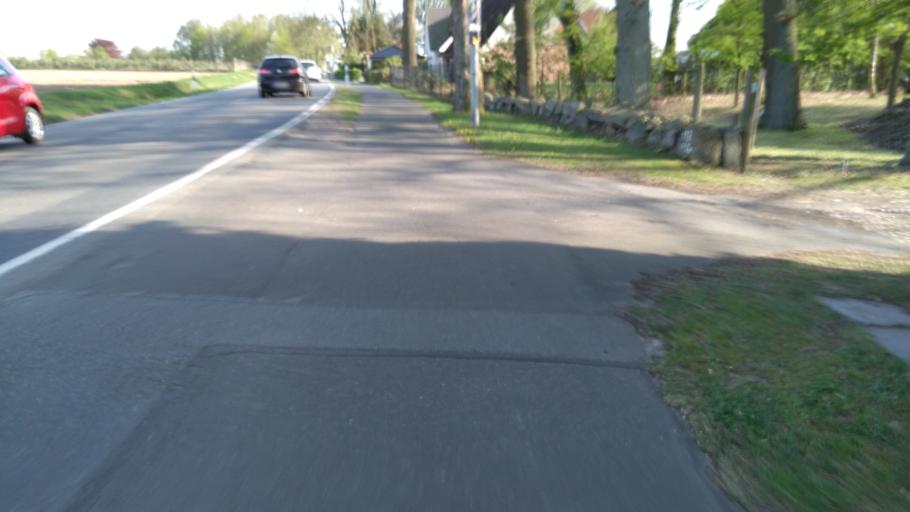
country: DE
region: Lower Saxony
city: Buxtehude
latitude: 53.4376
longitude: 9.6923
